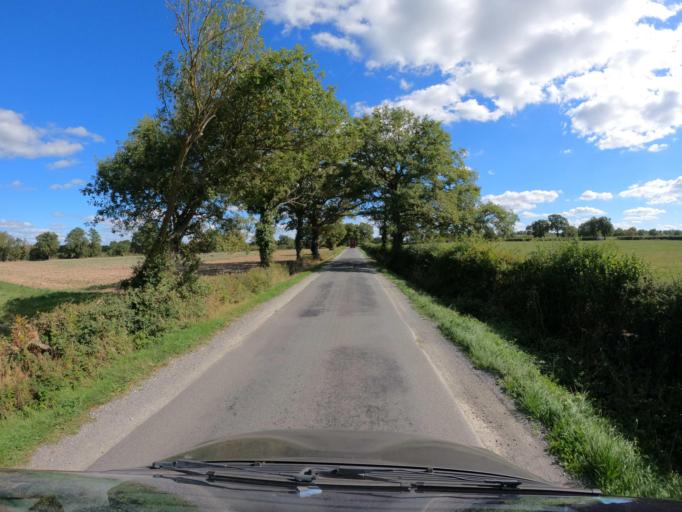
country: FR
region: Auvergne
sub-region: Departement de l'Allier
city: Doyet
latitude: 46.3923
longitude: 2.7566
